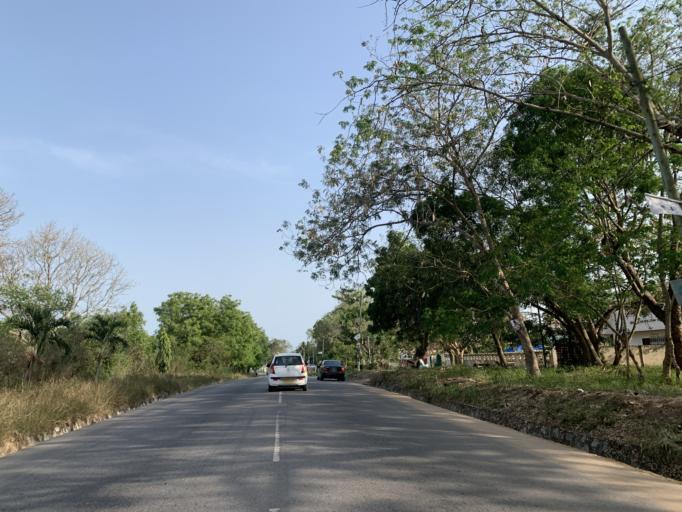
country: GH
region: Central
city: Winneba
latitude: 5.3695
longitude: -0.6380
